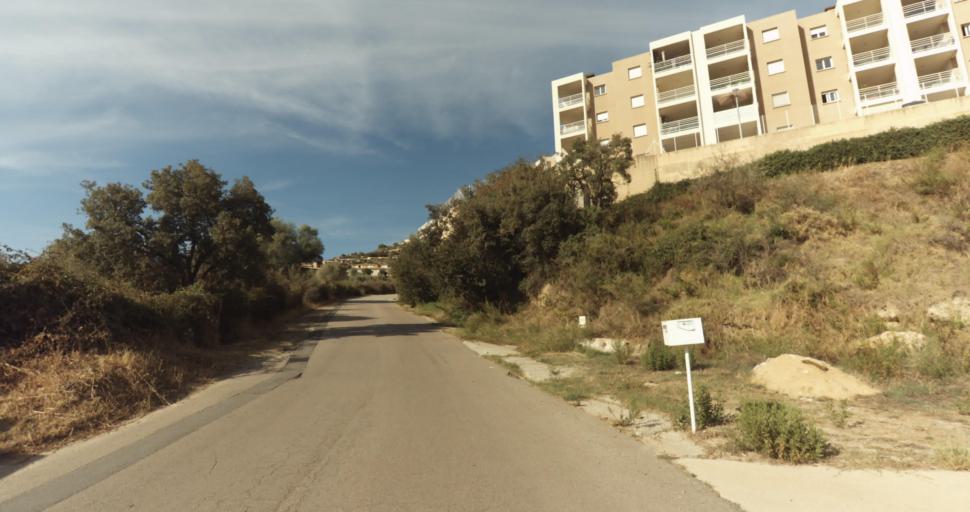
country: FR
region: Corsica
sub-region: Departement de la Corse-du-Sud
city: Afa
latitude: 41.9329
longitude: 8.7909
